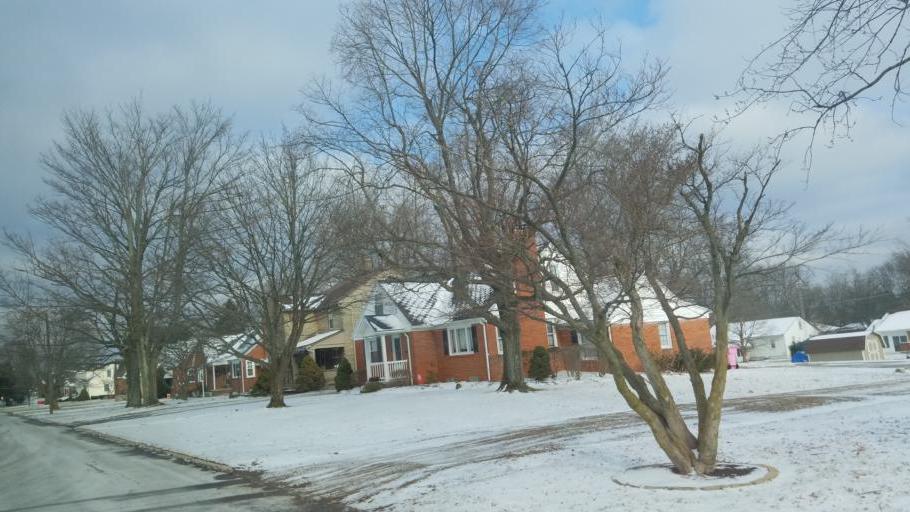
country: US
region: Ohio
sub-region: Richland County
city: Mansfield
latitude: 40.7303
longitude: -82.5332
